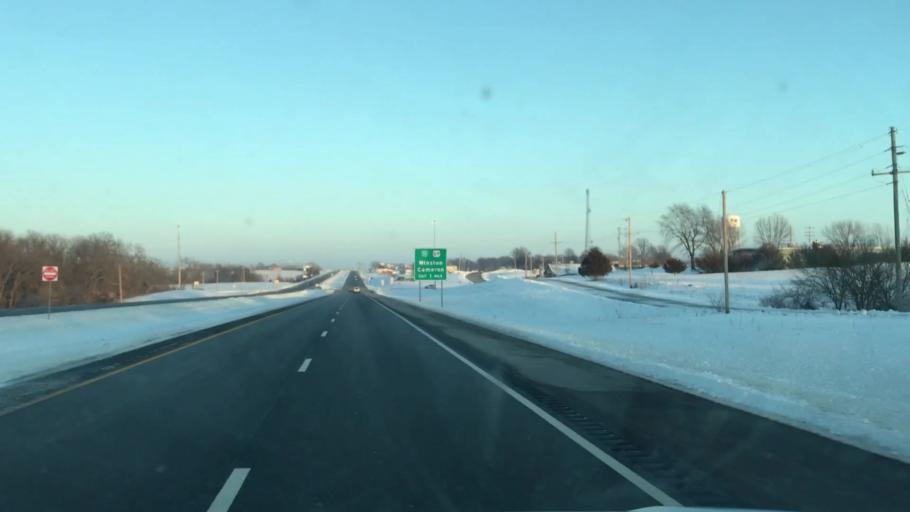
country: US
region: Missouri
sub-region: Clinton County
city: Cameron
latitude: 39.7538
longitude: -94.2568
